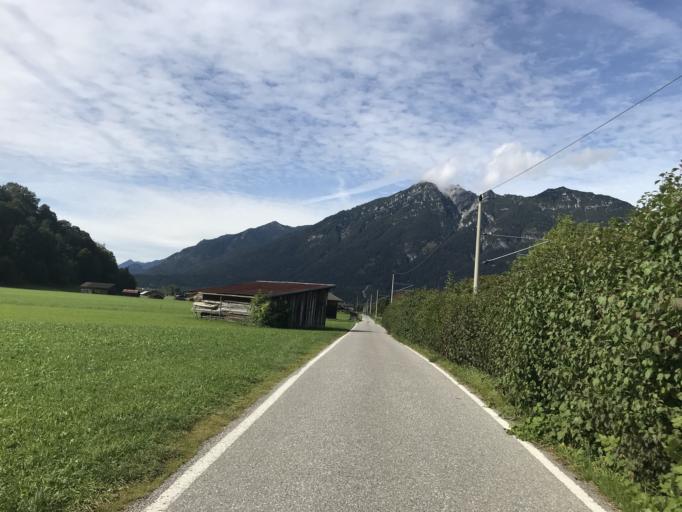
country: DE
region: Bavaria
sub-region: Upper Bavaria
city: Garmisch-Partenkirchen
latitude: 47.4835
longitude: 11.1100
